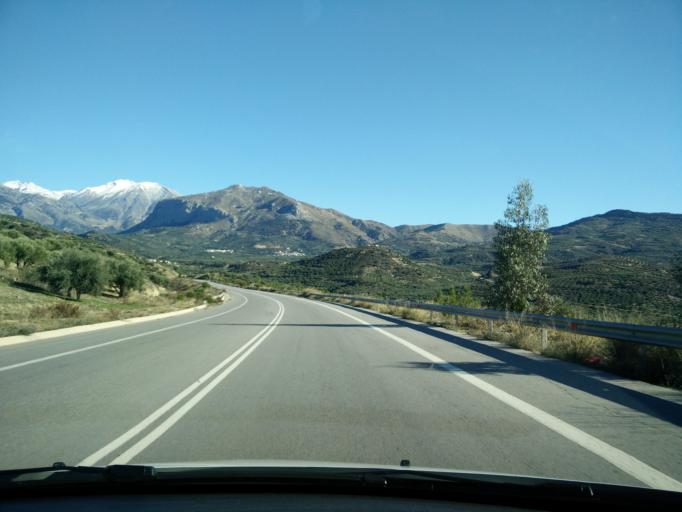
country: GR
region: Crete
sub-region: Nomos Irakleiou
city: Arkalochori
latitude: 35.0804
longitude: 25.3183
